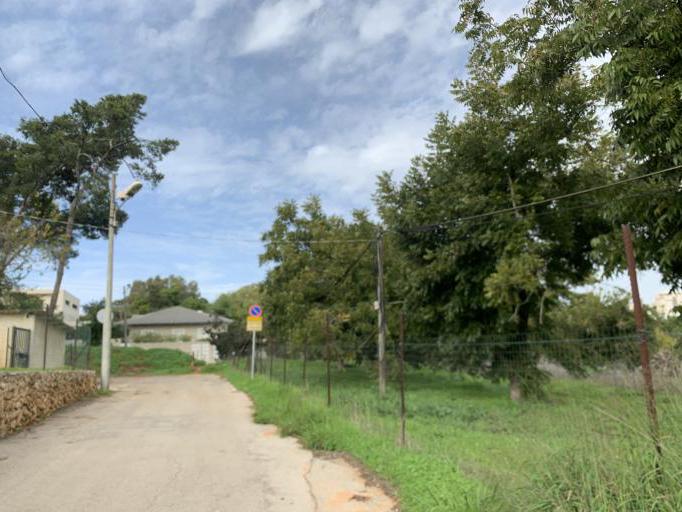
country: IL
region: Central District
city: Hod HaSharon
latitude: 32.1541
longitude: 34.9010
